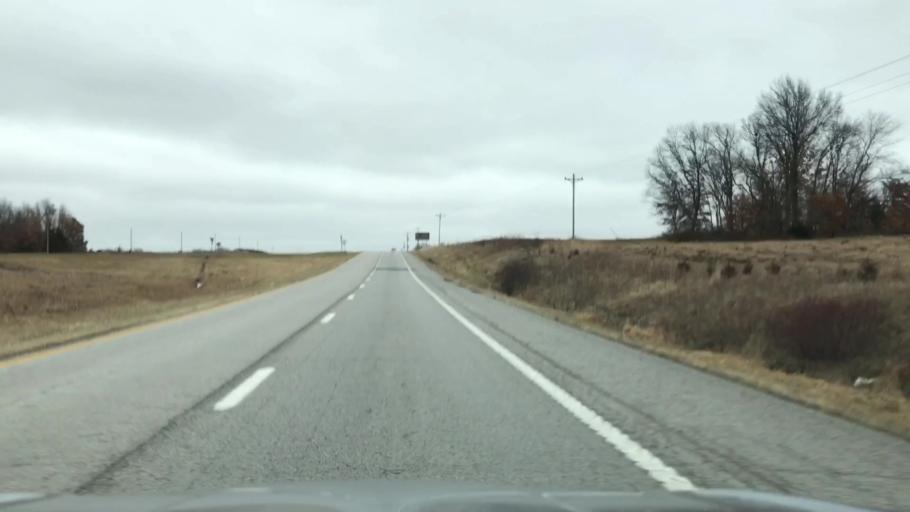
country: US
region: Missouri
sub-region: Linn County
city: Linneus
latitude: 39.7782
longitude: -93.1857
